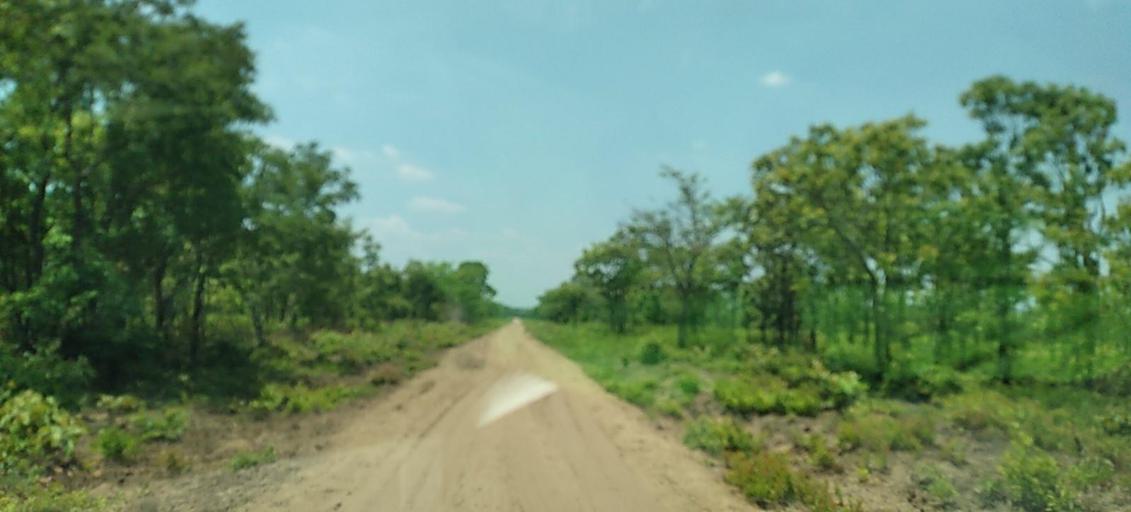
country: CD
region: Katanga
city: Kolwezi
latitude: -11.3391
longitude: 25.2209
